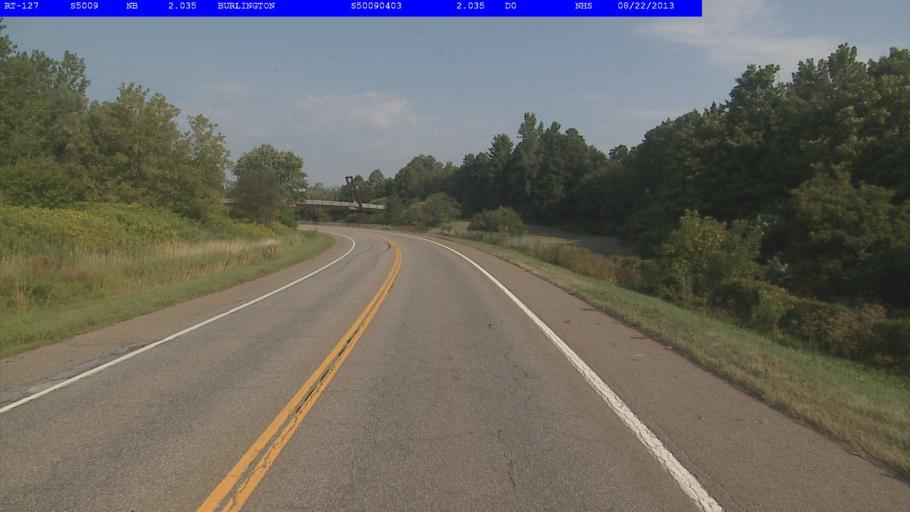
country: US
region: Vermont
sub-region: Chittenden County
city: Burlington
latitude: 44.5135
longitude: -73.2349
